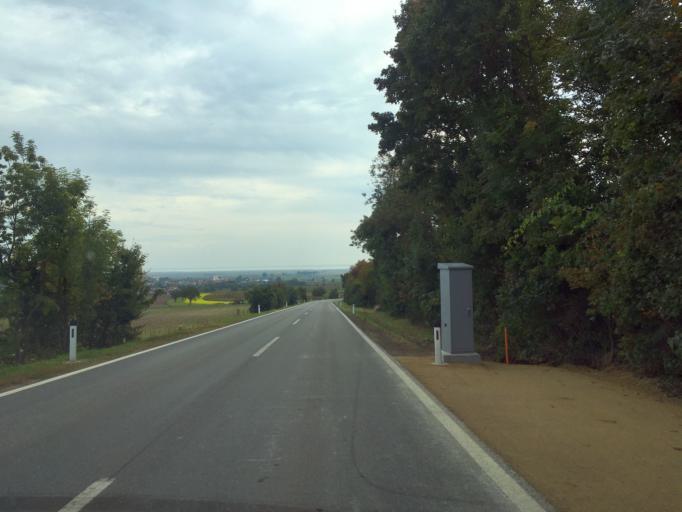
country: AT
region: Burgenland
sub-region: Eisenstadt-Umgebung
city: Breitenbrunn
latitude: 47.9581
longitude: 16.7363
